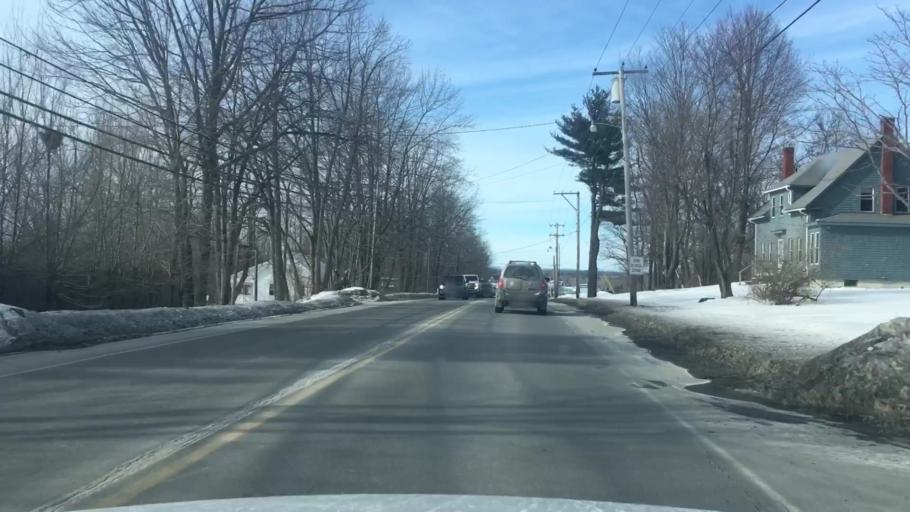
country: US
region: Maine
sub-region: Penobscot County
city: Bangor
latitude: 44.8321
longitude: -68.7875
